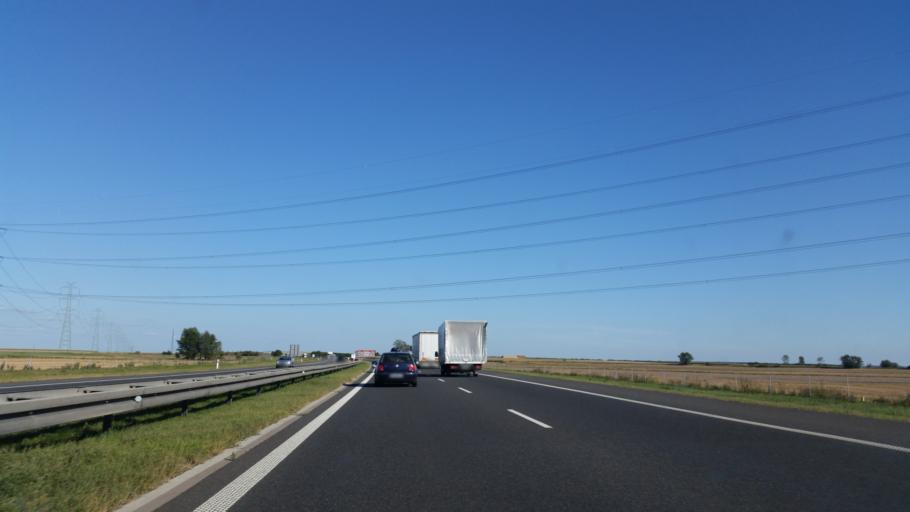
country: PL
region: Opole Voivodeship
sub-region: Powiat brzeski
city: Olszanka
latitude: 50.7422
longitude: 17.4581
